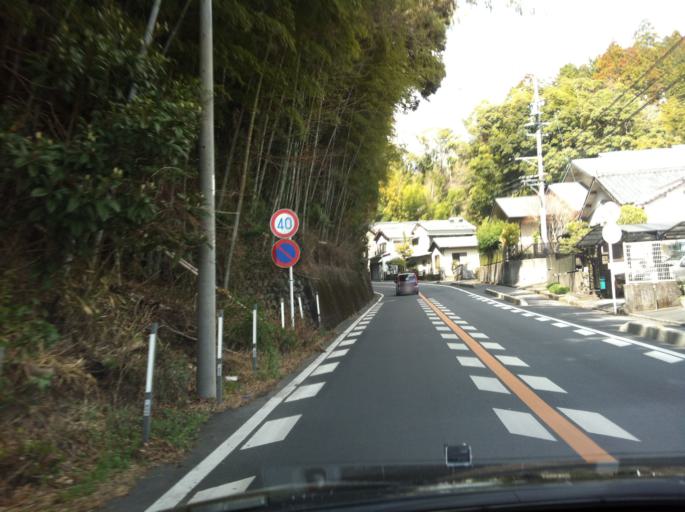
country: JP
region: Shizuoka
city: Shimada
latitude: 34.8454
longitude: 138.1748
